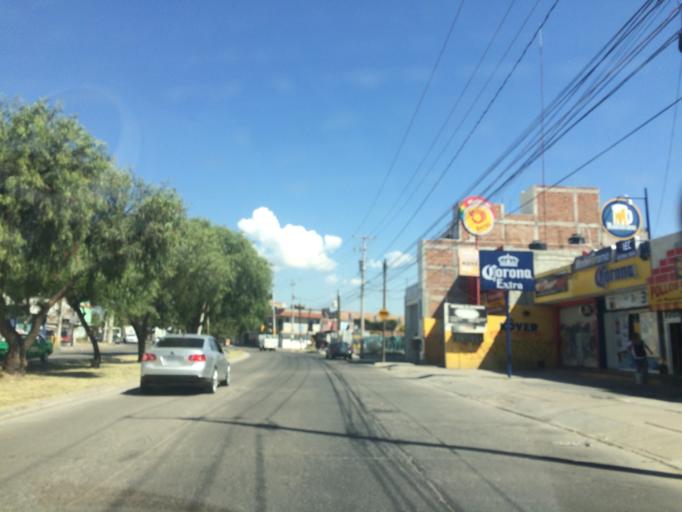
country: MX
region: Guanajuato
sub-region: Leon
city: San Jose de Duran (Los Troncoso)
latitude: 21.0811
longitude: -101.6509
